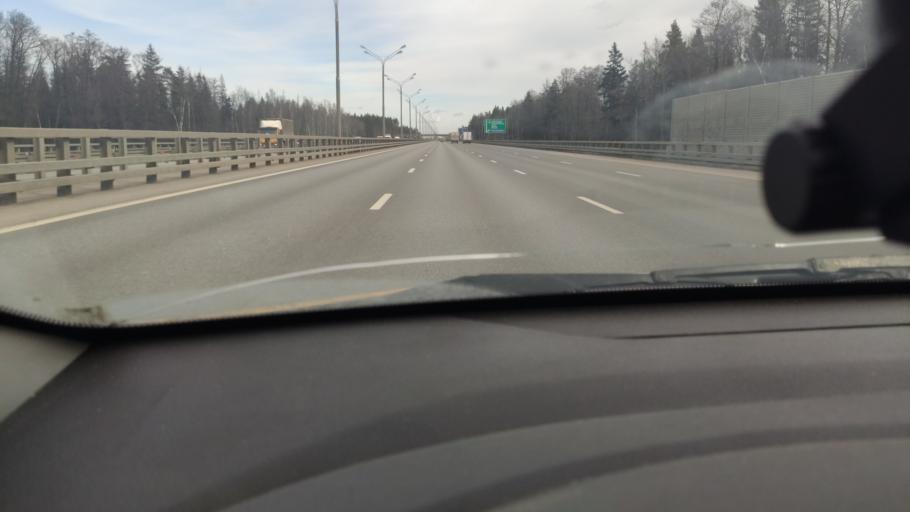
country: RU
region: Moskovskaya
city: Krasnoznamensk
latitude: 55.6070
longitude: 37.0391
